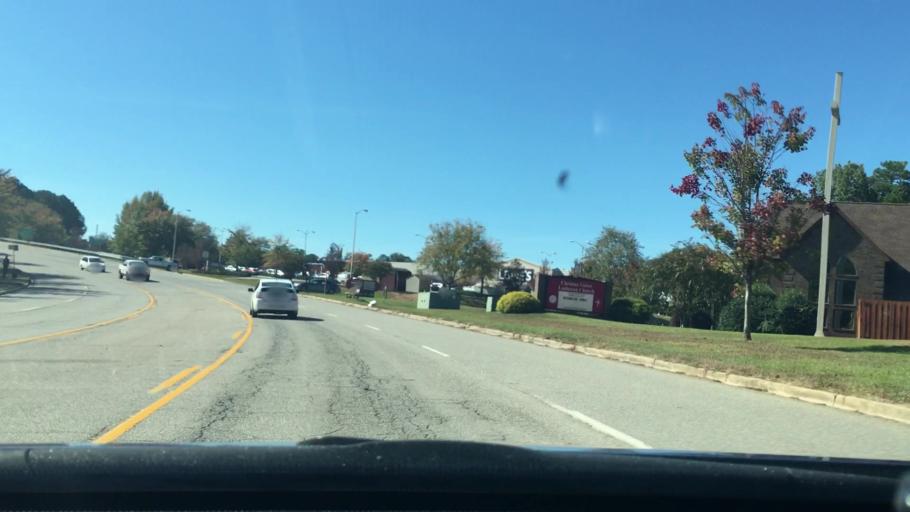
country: US
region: South Carolina
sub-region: Lexington County
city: Seven Oaks
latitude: 34.0806
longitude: -81.1494
